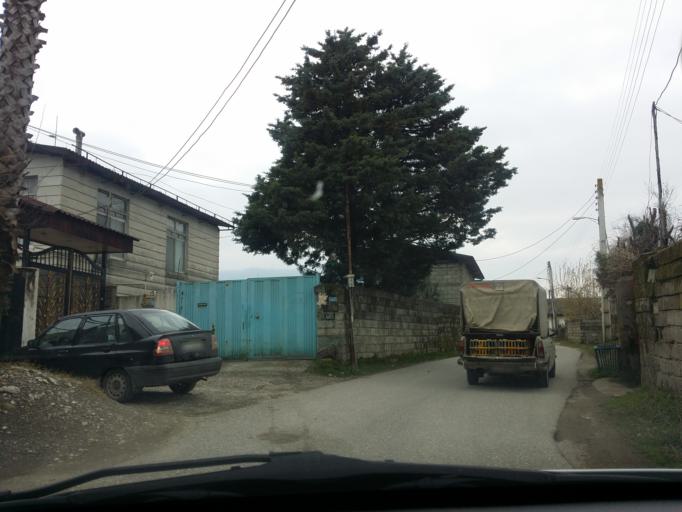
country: IR
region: Mazandaran
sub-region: Nowshahr
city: Nowshahr
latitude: 36.6495
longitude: 51.4781
